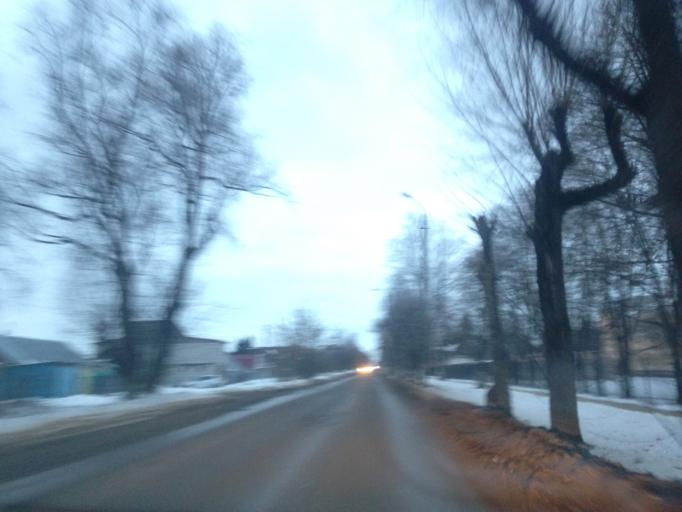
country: RU
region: Tula
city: Shchekino
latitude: 54.0035
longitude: 37.5270
